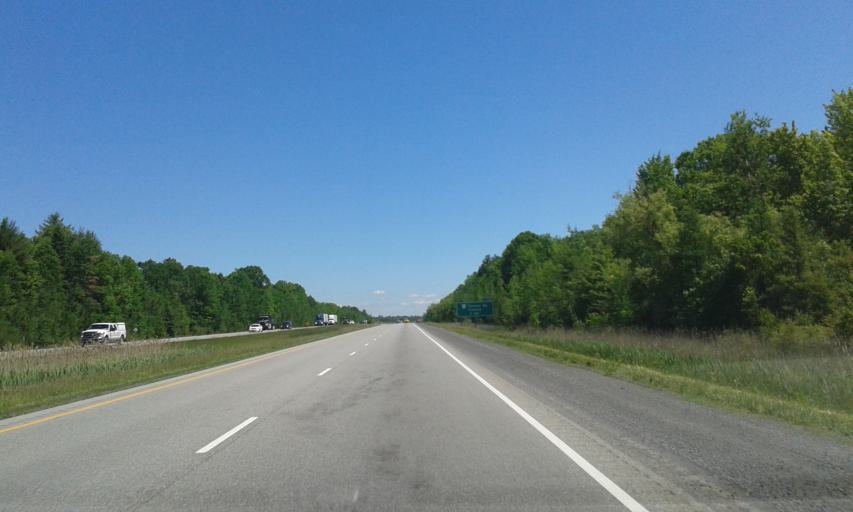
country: US
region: New York
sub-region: St. Lawrence County
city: Ogdensburg
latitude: 44.8486
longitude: -75.3441
